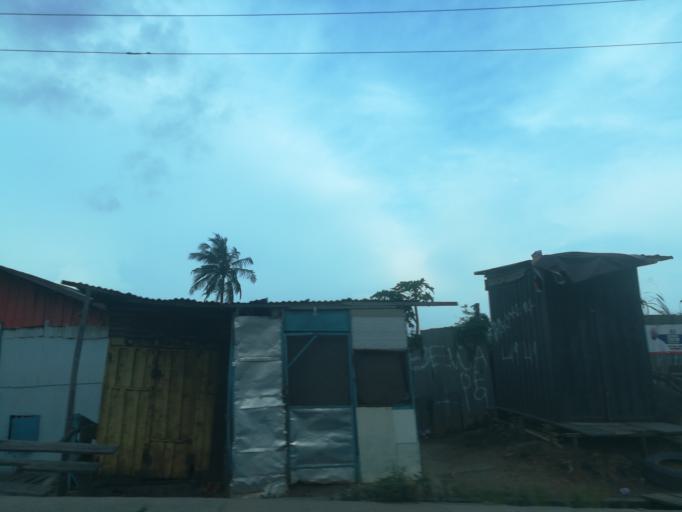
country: NG
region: Lagos
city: Ebute Ikorodu
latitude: 6.6179
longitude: 3.4753
